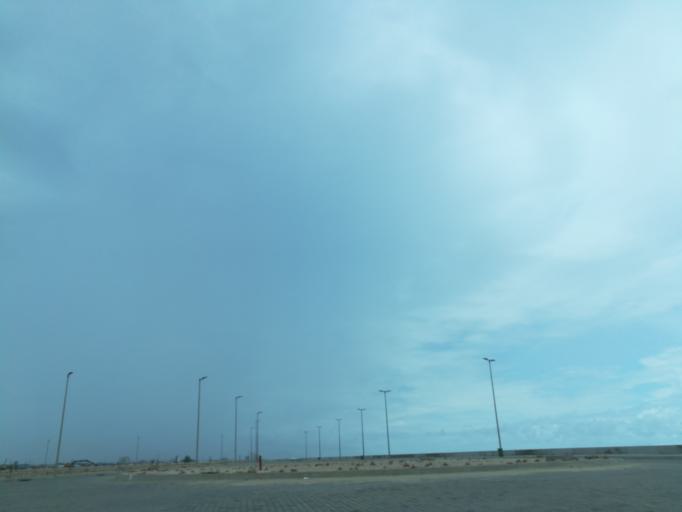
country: NG
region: Lagos
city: Ikoyi
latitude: 6.4060
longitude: 3.4188
